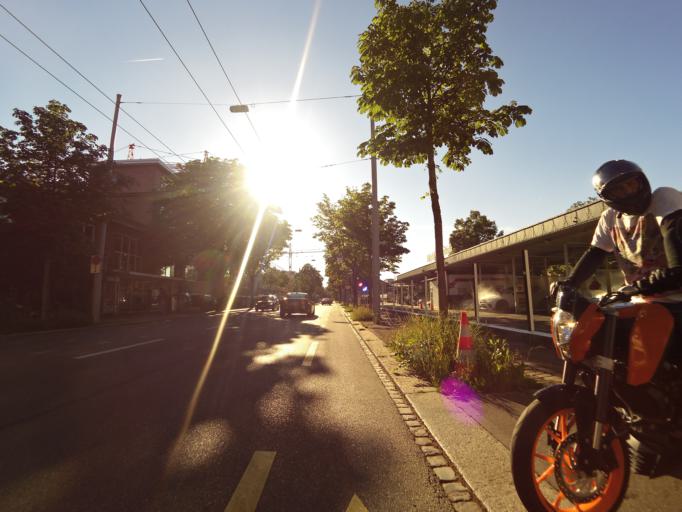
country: CH
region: Zurich
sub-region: Bezirk Zuerich
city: Zuerich (Kreis 4) / Hard
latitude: 47.3874
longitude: 8.5007
